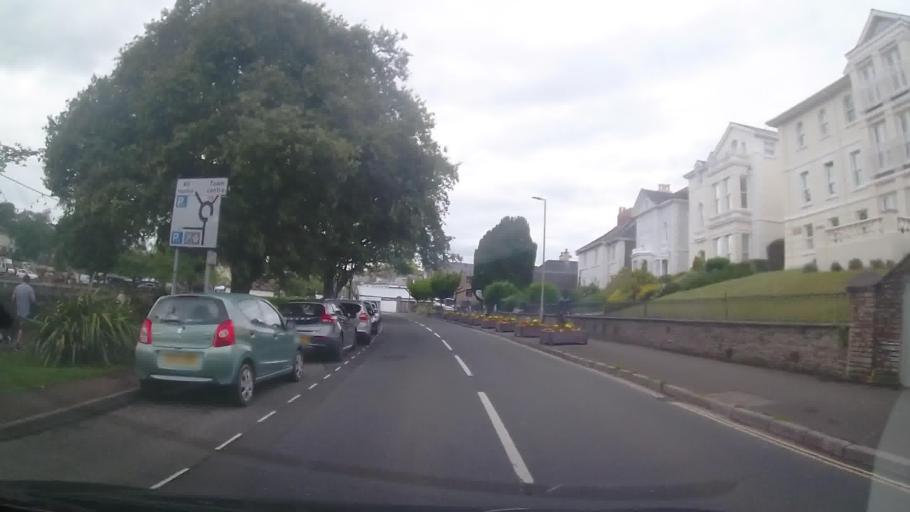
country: GB
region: England
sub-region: Devon
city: Kingsbridge
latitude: 50.2820
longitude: -3.7752
